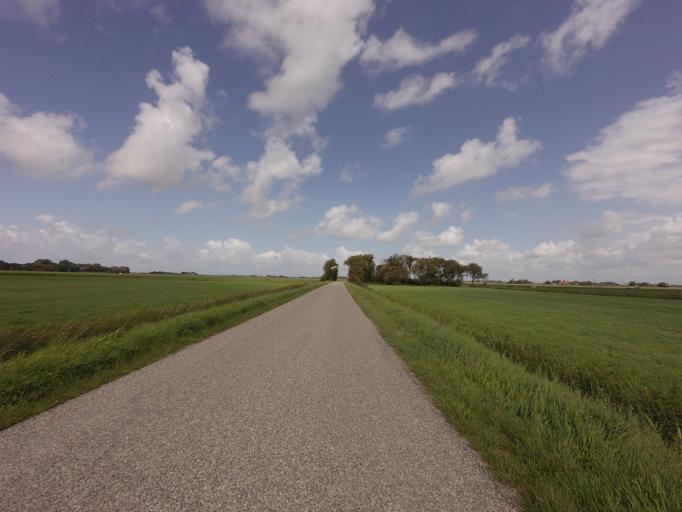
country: NL
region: Friesland
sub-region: Gemeente Franekeradeel
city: Sexbierum
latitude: 53.1595
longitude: 5.4830
